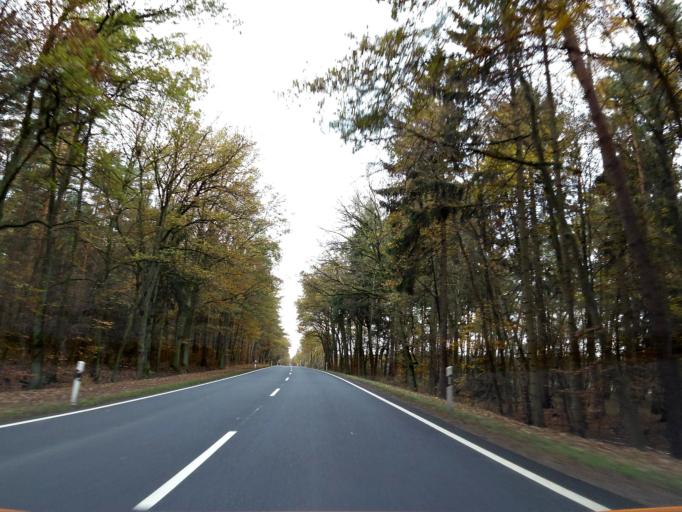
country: DE
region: Lower Saxony
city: Schnega
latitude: 52.9186
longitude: 10.8820
